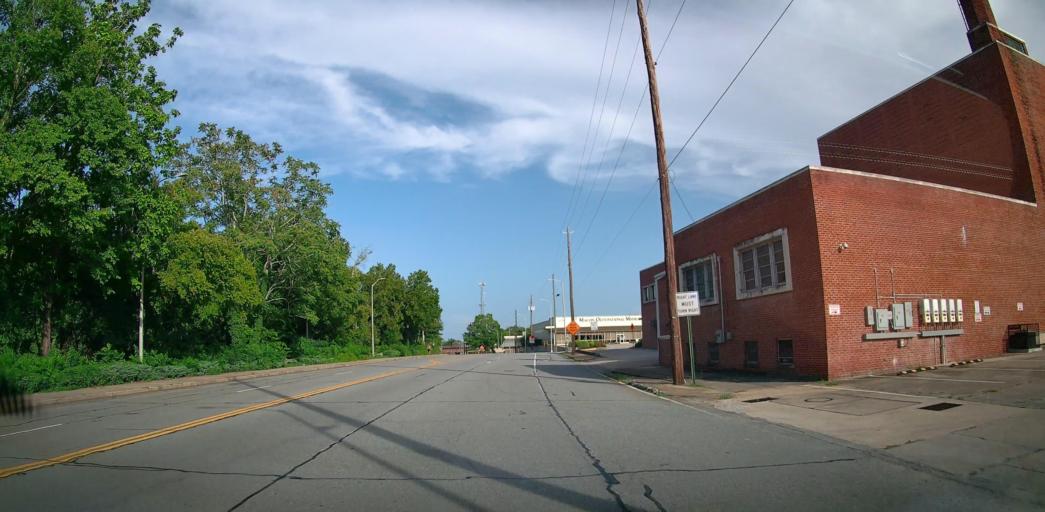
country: US
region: Georgia
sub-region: Bibb County
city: Macon
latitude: 32.8401
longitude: -83.6250
